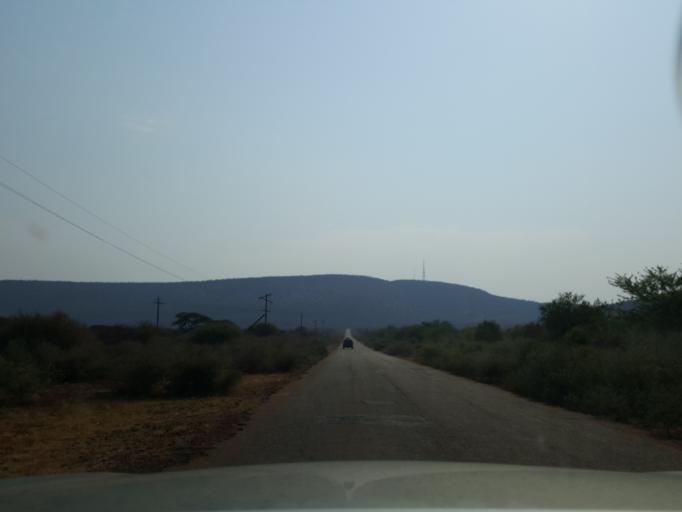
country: BW
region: South East
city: Lobatse
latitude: -25.2929
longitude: 25.8502
